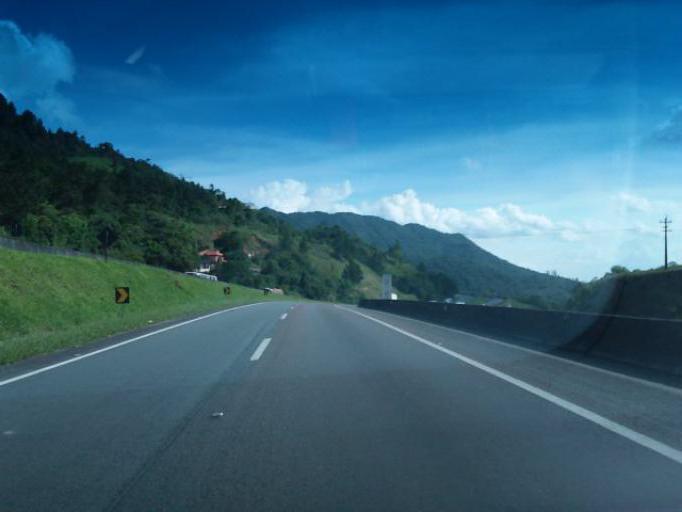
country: BR
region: Parana
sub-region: Campina Grande Do Sul
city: Campina Grande do Sul
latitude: -25.1556
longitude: -48.8614
